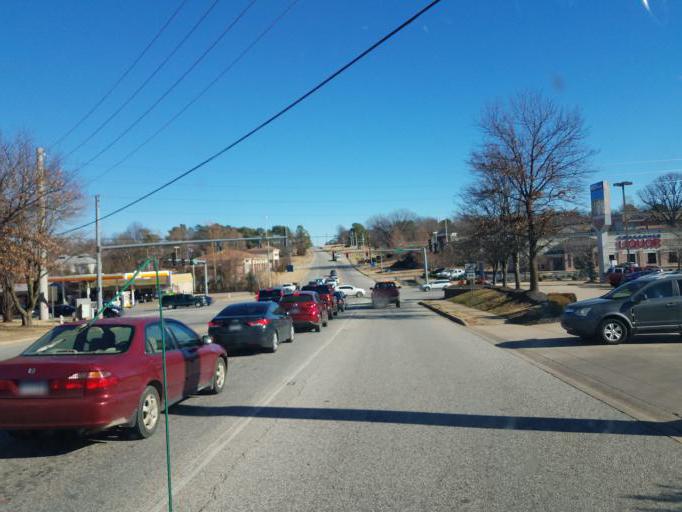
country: US
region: Arkansas
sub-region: Washington County
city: Fayetteville
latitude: 36.0873
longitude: -94.1222
